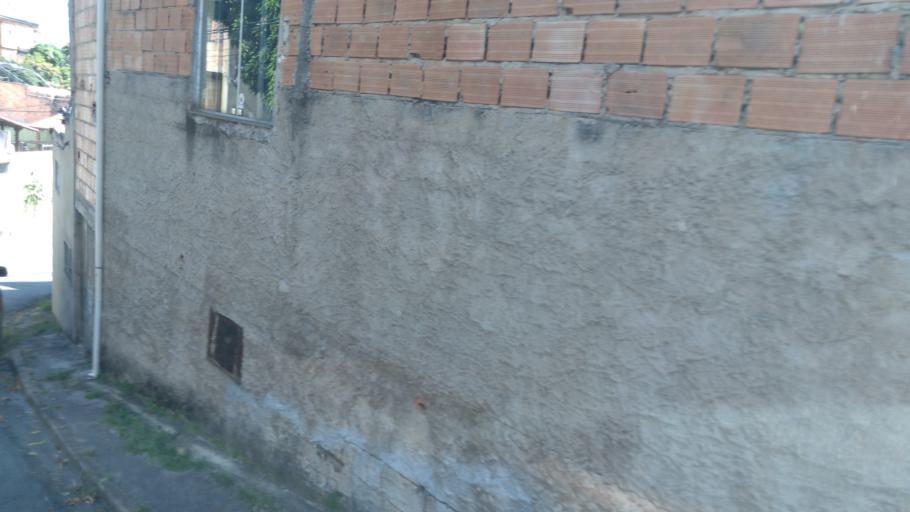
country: BR
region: Minas Gerais
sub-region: Belo Horizonte
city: Belo Horizonte
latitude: -19.8494
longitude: -43.9110
